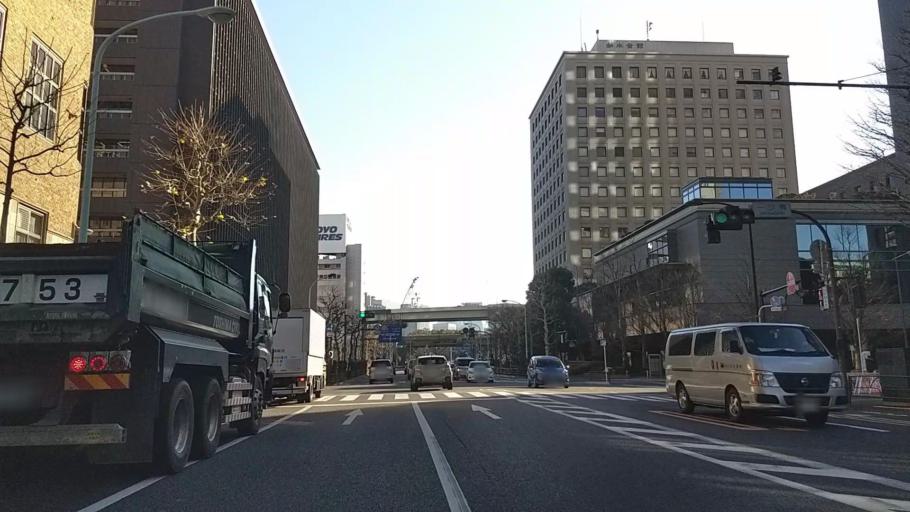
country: JP
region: Tokyo
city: Tokyo
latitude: 35.6931
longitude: 139.7588
